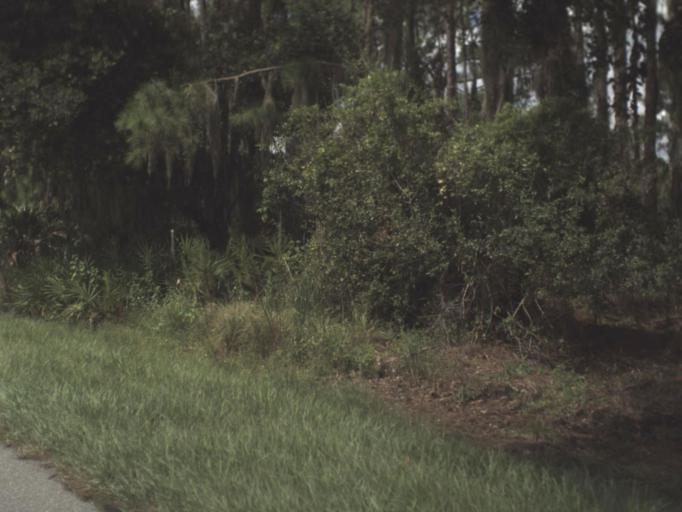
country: US
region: Florida
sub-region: Hillsborough County
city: Balm
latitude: 27.6277
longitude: -82.0760
